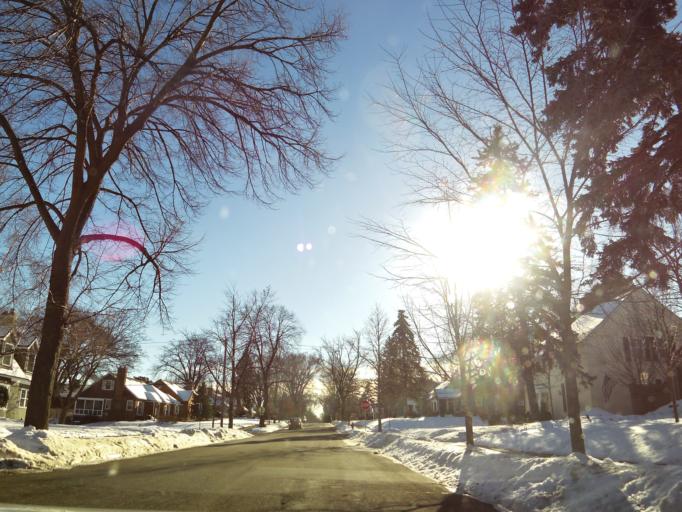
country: US
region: Minnesota
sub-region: Hennepin County
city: Saint Louis Park
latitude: 44.9329
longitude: -93.3342
